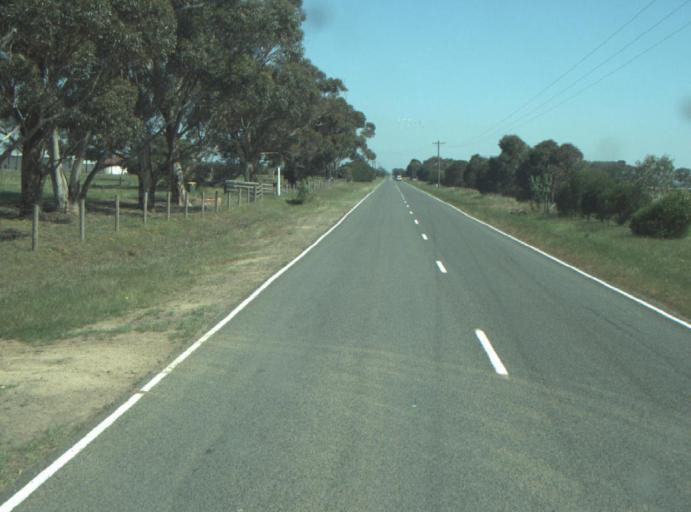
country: AU
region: Victoria
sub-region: Greater Geelong
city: Lara
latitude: -37.9758
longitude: 144.4048
